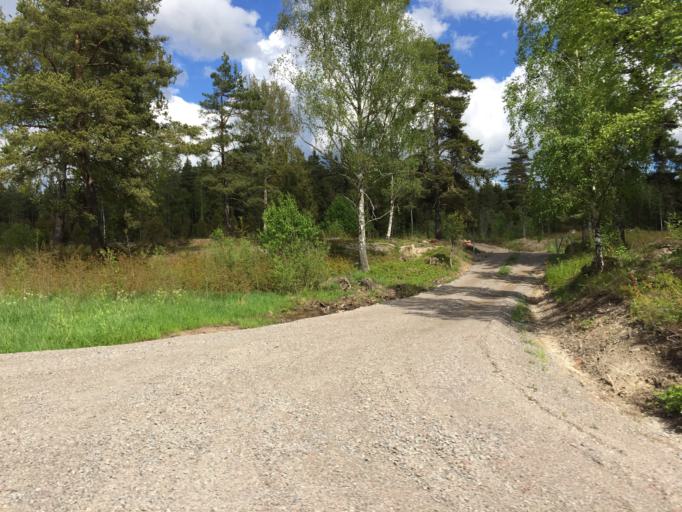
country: SE
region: OEstergoetland
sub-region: Finspangs Kommun
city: Finspang
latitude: 58.6916
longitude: 15.7514
